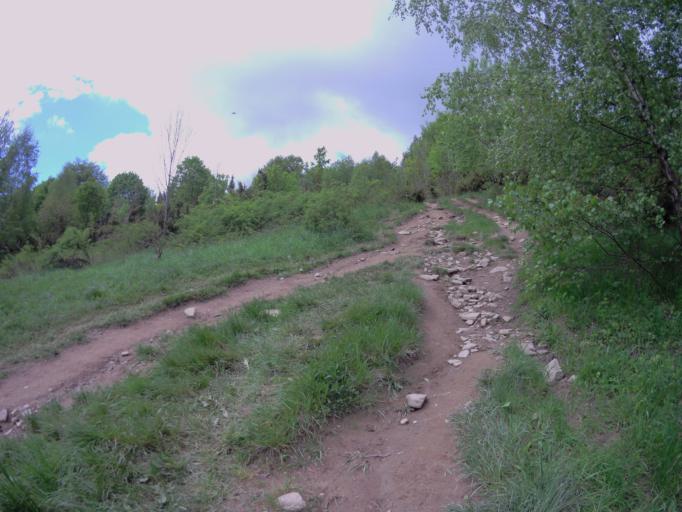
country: PL
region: Subcarpathian Voivodeship
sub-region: Powiat bieszczadzki
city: Lutowiska
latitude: 49.1468
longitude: 22.5612
